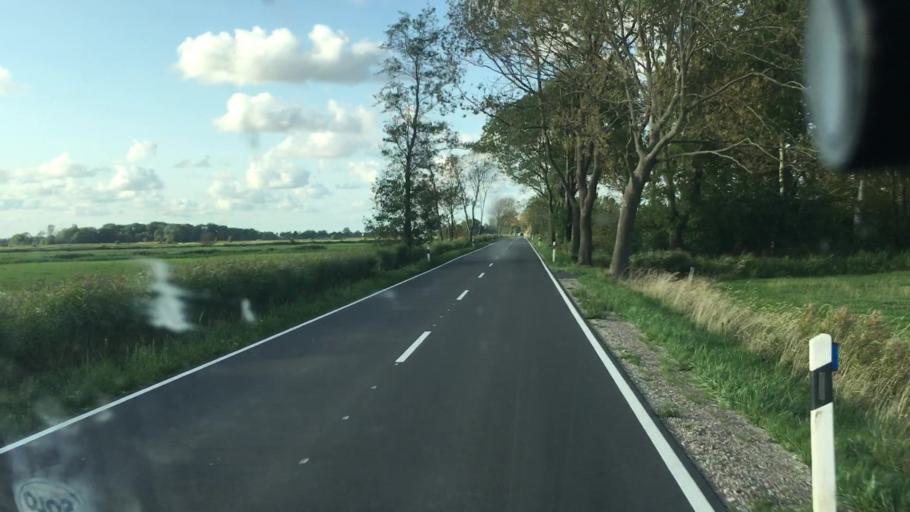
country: DE
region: Lower Saxony
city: Jever
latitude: 53.6321
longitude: 7.8615
